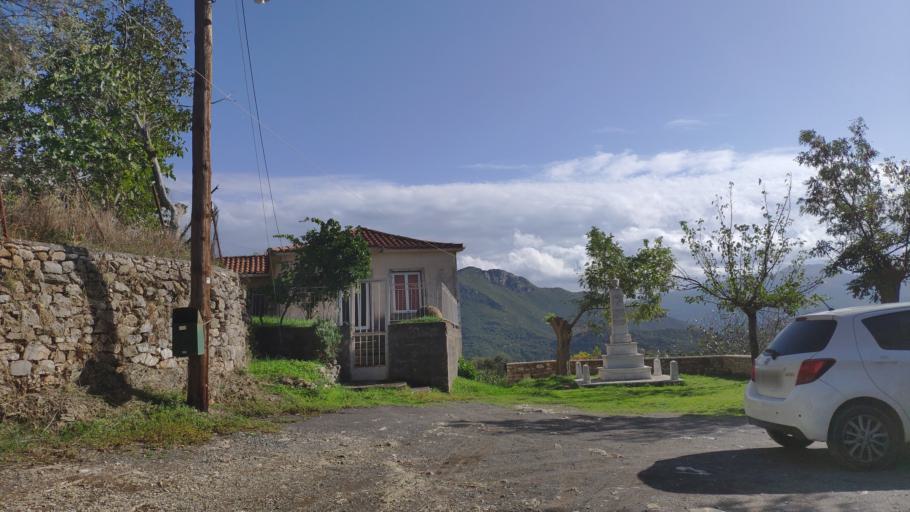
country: GR
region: Peloponnese
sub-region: Nomos Arkadias
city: Dimitsana
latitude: 37.5578
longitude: 21.9900
